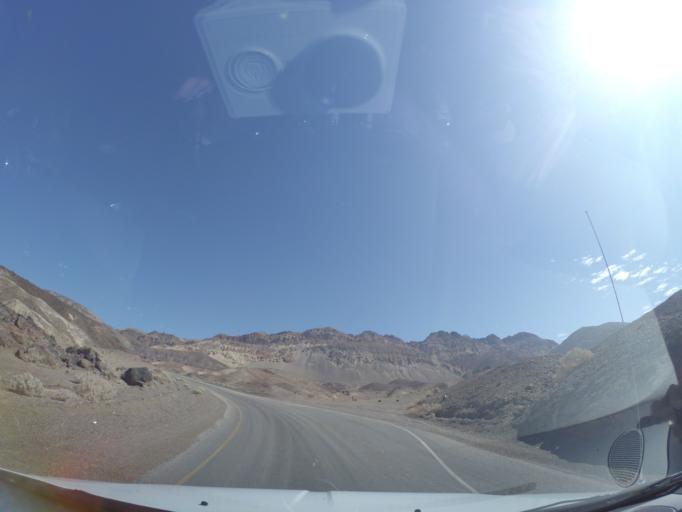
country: US
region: Nevada
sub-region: Nye County
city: Beatty
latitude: 36.3724
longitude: -116.8213
